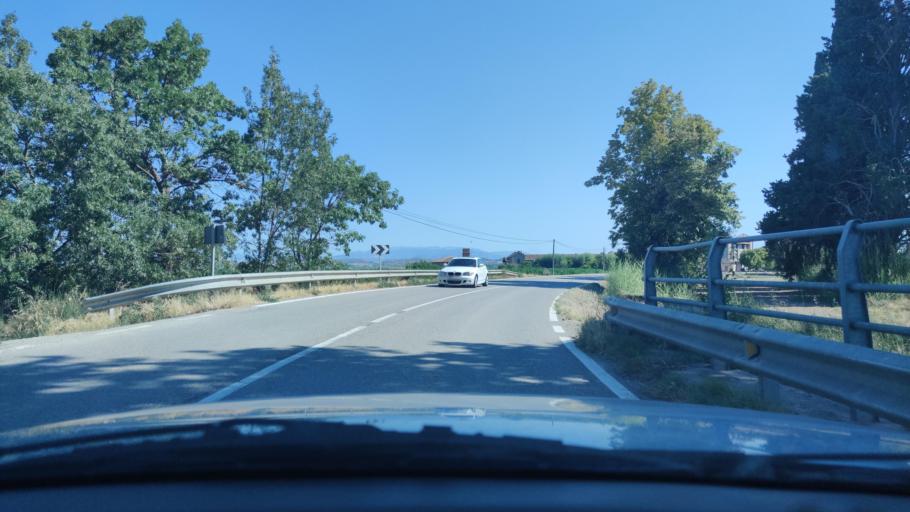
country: ES
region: Catalonia
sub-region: Provincia de Lleida
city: Bellcaire d'Urgell
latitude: 41.7291
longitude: 0.9263
